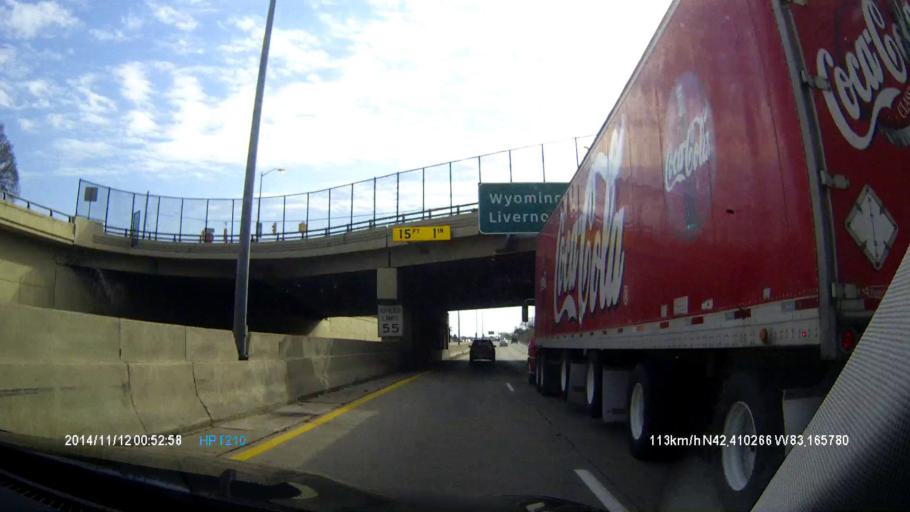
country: US
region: Michigan
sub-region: Oakland County
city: Oak Park
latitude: 42.4101
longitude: -83.1660
